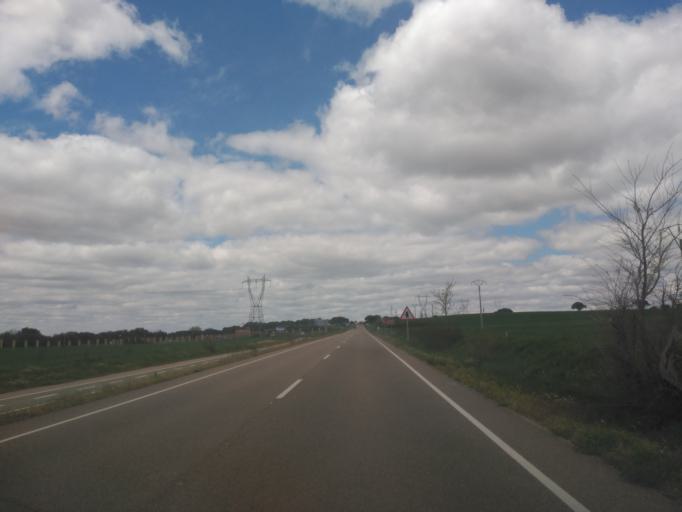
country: ES
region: Castille and Leon
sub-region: Provincia de Salamanca
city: Florida de Liebana
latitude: 41.0283
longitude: -5.7273
